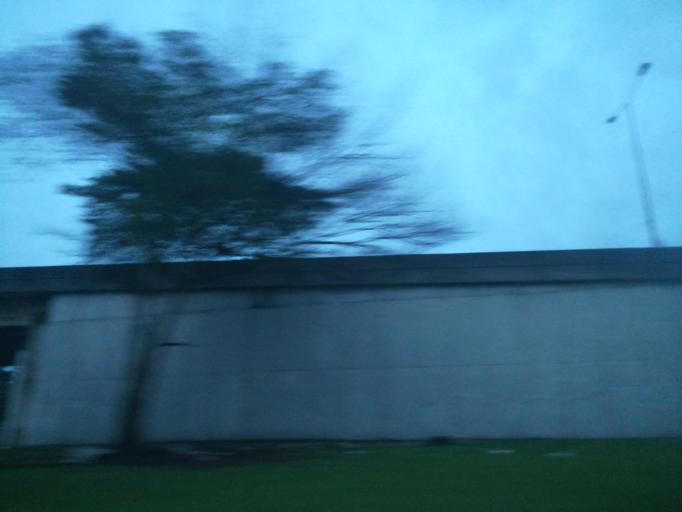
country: NG
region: Rivers
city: Port Harcourt
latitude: 4.7868
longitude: 7.0041
